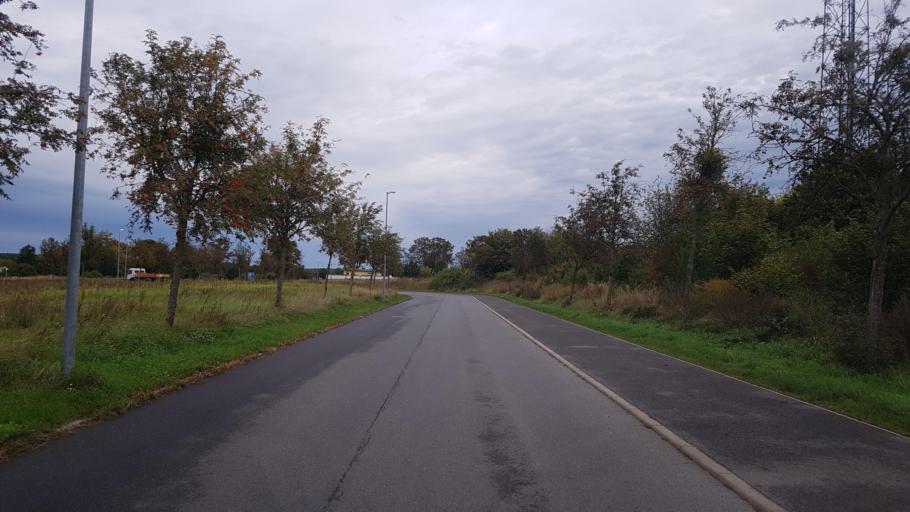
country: DE
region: Brandenburg
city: Golssen
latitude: 51.9781
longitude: 13.5772
